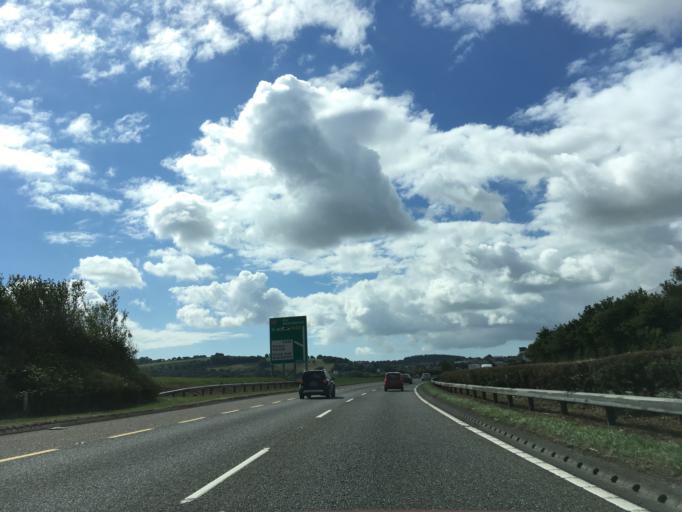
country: IE
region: Munster
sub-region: County Cork
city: Passage West
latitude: 51.8903
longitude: -8.3907
